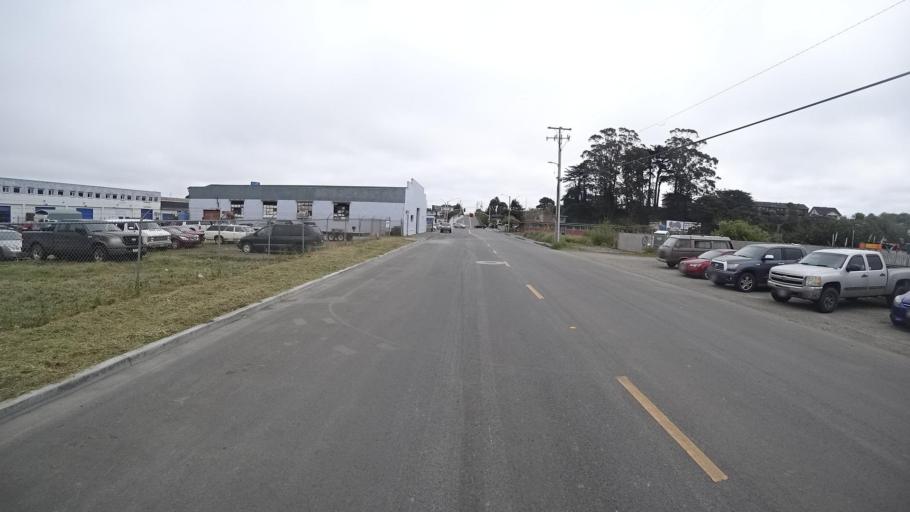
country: US
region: California
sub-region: Humboldt County
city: Bayview
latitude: 40.7891
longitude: -124.1814
